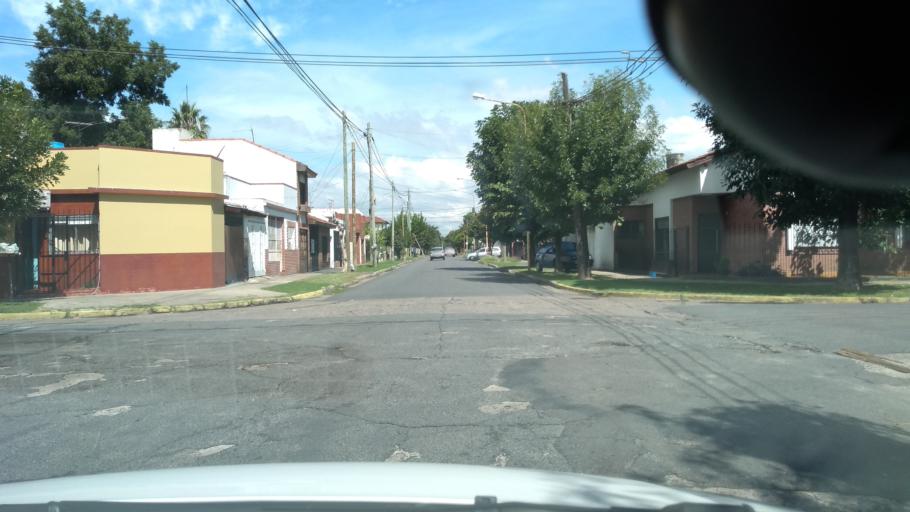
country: AR
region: Buenos Aires
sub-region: Partido de Moron
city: Moron
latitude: -34.6681
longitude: -58.6001
